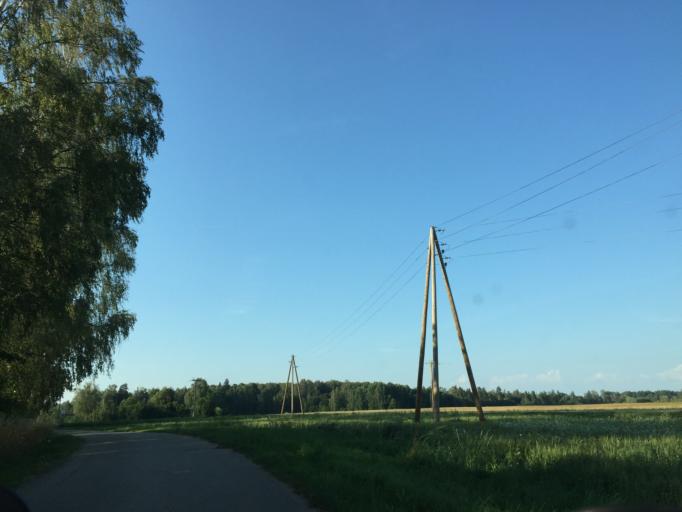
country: LV
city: Tervete
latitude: 56.4258
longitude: 23.5420
